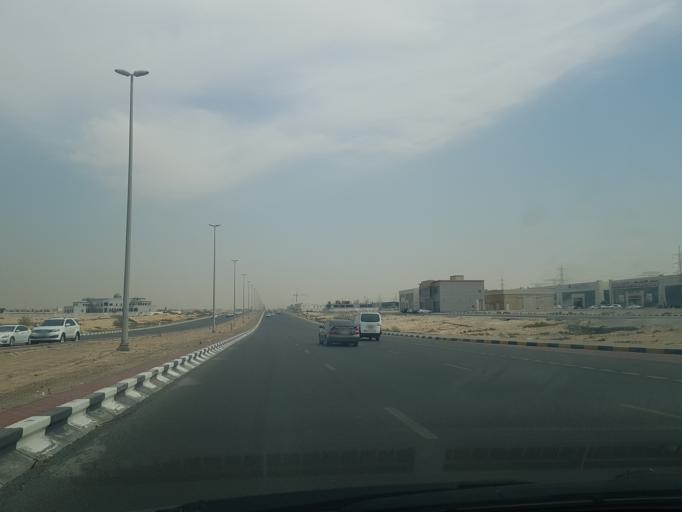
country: AE
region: Ash Shariqah
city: Sharjah
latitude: 25.2618
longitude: 55.5040
